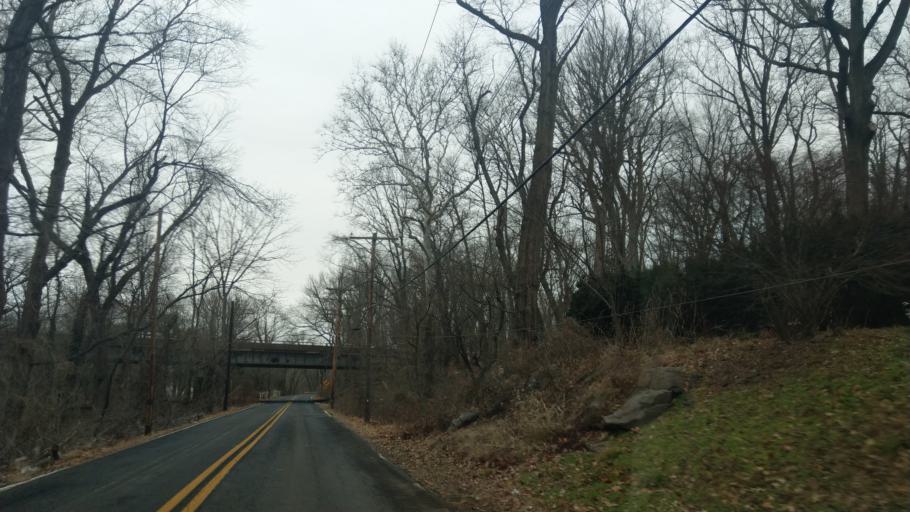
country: US
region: Pennsylvania
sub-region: Bucks County
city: Hulmeville
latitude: 40.1281
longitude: -74.8999
